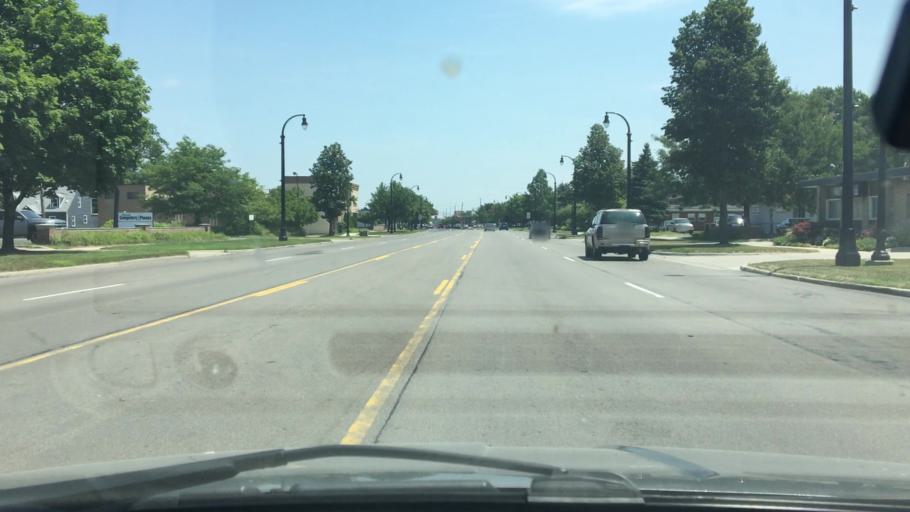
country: US
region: Michigan
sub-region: Wayne County
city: Redford
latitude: 42.3696
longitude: -83.3184
